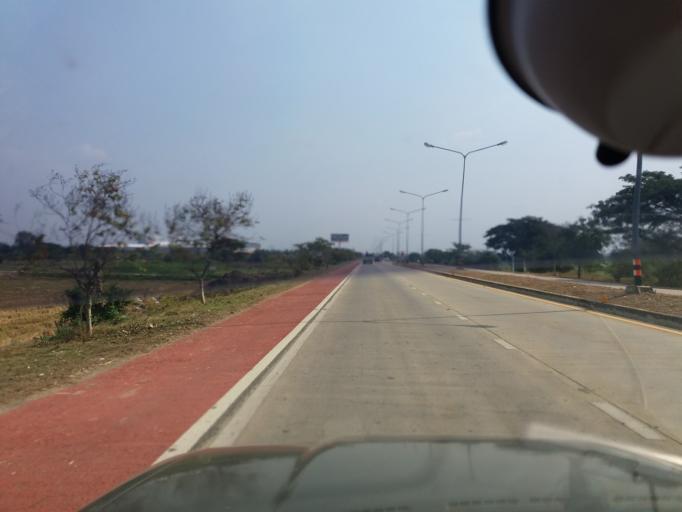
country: TH
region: Sing Buri
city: Sing Buri
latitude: 14.8774
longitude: 100.3941
